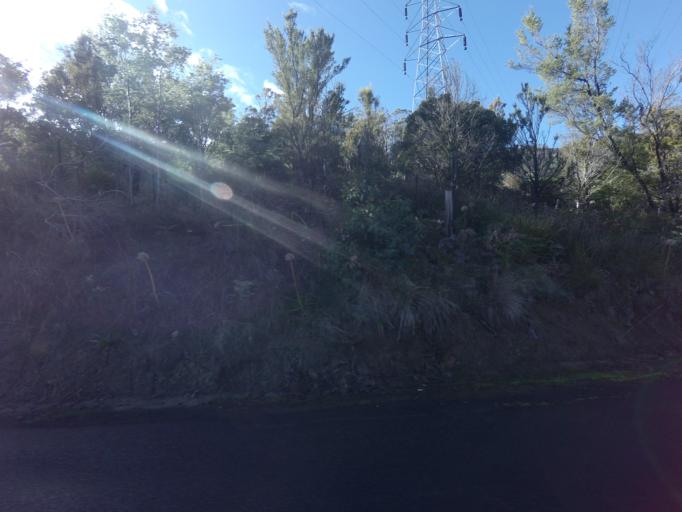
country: AU
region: Tasmania
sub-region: Glenorchy
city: Berriedale
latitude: -42.8132
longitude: 147.1746
